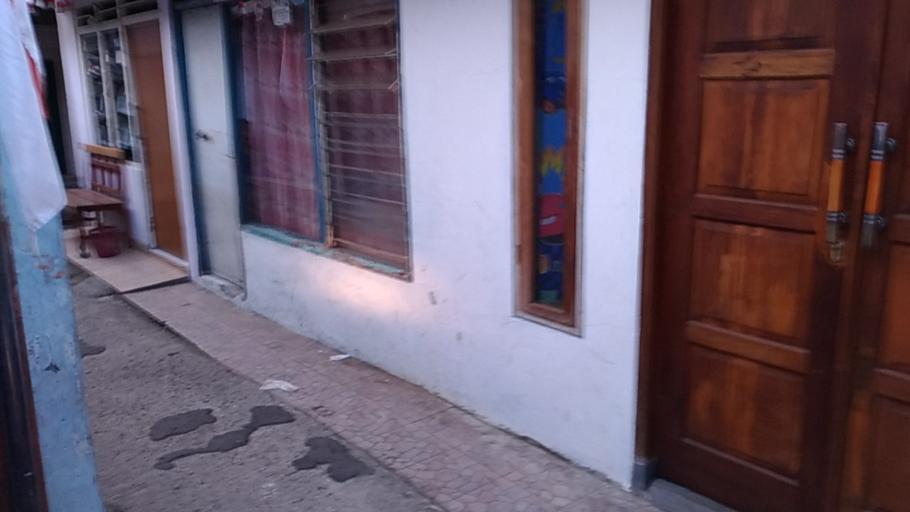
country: ID
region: West Java
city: Depok
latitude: -6.3769
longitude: 106.8613
